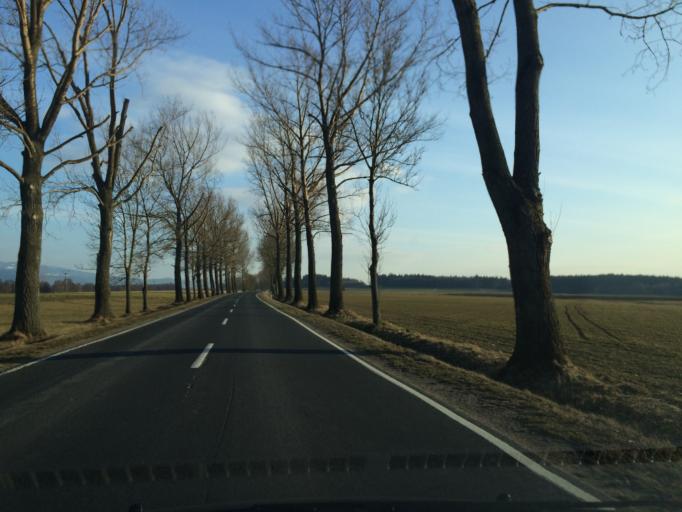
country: PL
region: Lower Silesian Voivodeship
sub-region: Powiat klodzki
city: Bystrzyca Klodzka
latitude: 50.2530
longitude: 16.6654
